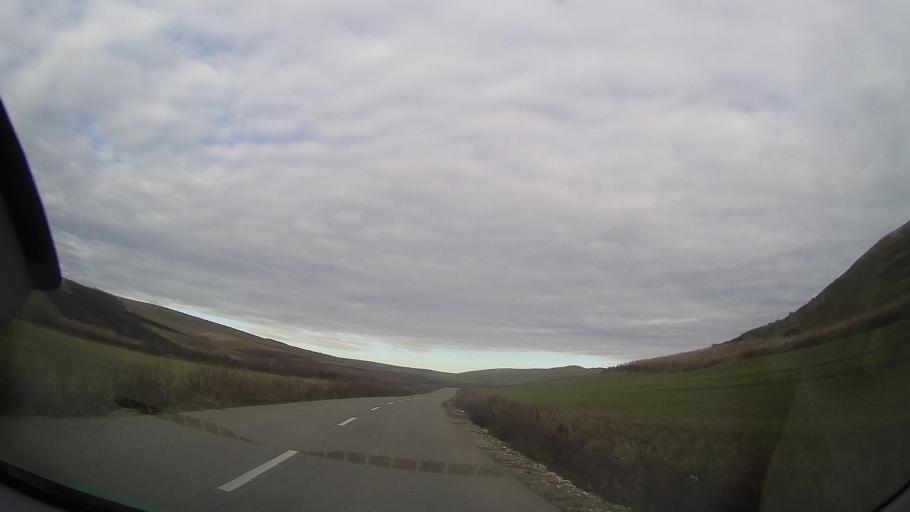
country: RO
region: Bistrita-Nasaud
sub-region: Comuna Silvasu de Campie
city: Silvasu de Campie
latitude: 46.7963
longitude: 24.2960
